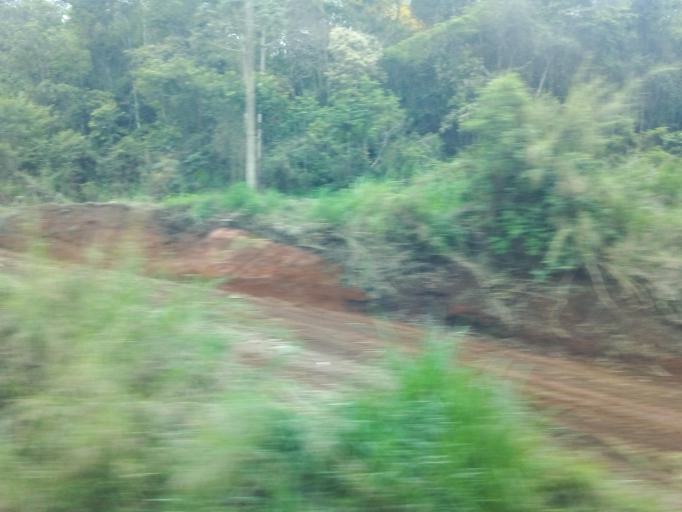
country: BR
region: Minas Gerais
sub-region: Rio Piracicaba
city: Rio Piracicaba
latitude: -19.8897
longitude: -43.1375
